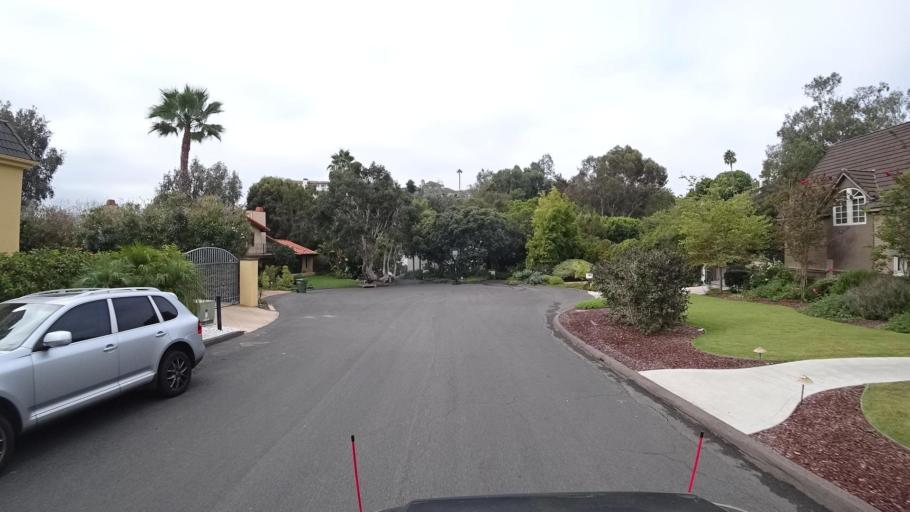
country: US
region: California
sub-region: San Diego County
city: Solana Beach
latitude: 32.9866
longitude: -117.2314
